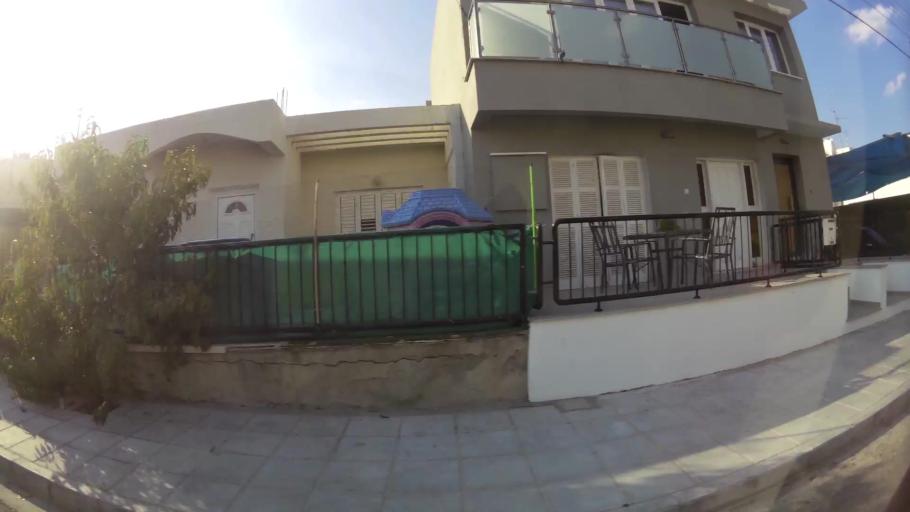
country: CY
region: Lefkosia
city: Kato Deftera
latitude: 35.1094
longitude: 33.2877
